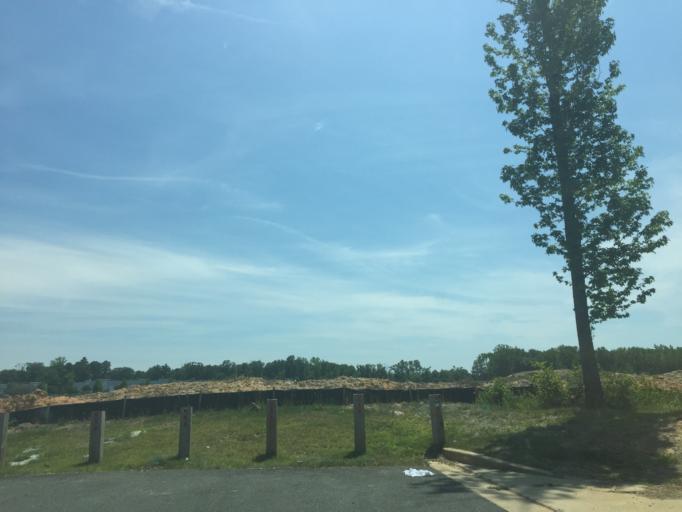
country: US
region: Maryland
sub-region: Baltimore County
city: Bowleys Quarters
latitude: 39.3503
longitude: -76.4132
